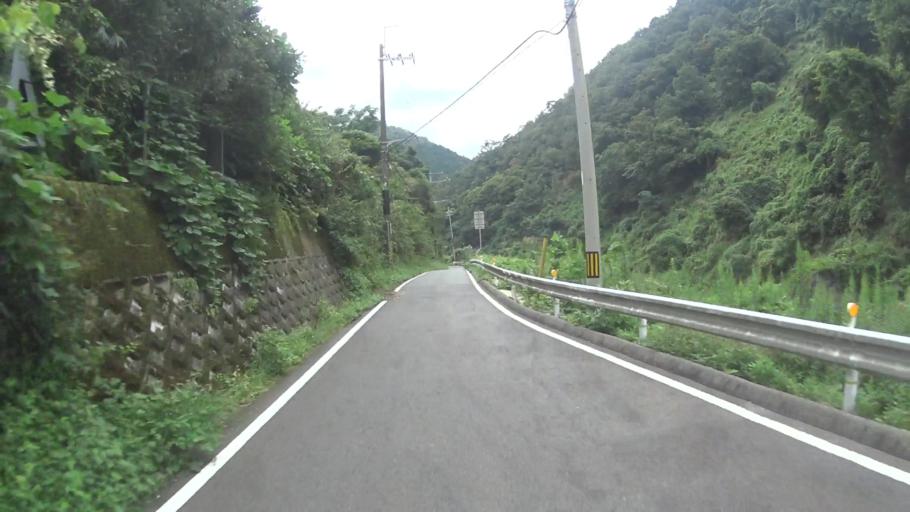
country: JP
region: Kyoto
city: Tanabe
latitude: 34.8028
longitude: 135.8328
